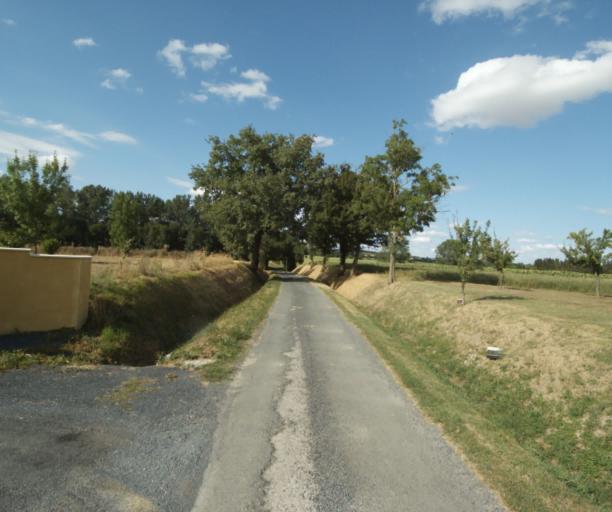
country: FR
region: Midi-Pyrenees
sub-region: Departement du Tarn
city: Puylaurens
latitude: 43.5314
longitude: 1.9822
